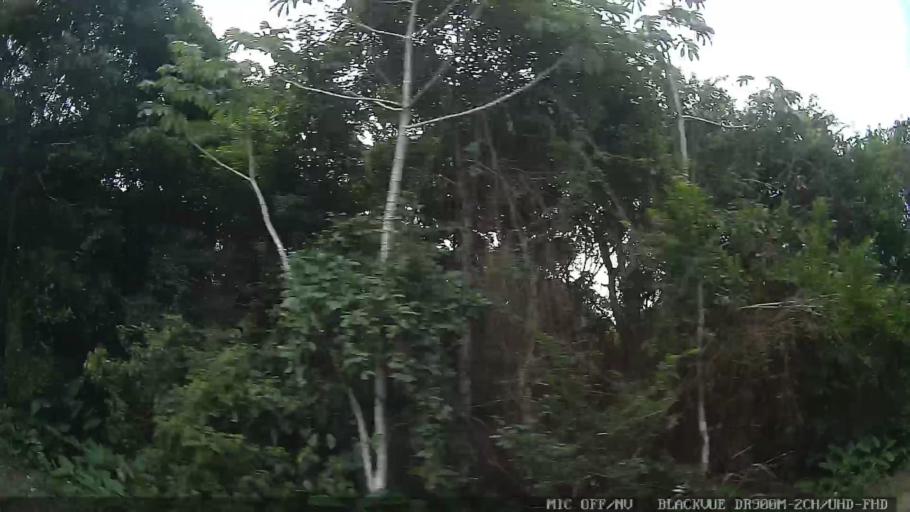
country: BR
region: Sao Paulo
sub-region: Iguape
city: Iguape
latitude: -24.6520
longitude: -47.4021
